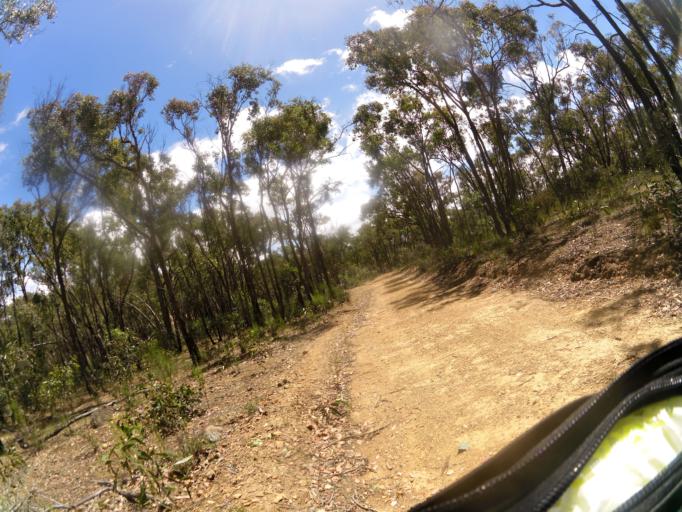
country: AU
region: Victoria
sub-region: Mount Alexander
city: Castlemaine
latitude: -37.0655
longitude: 144.2659
